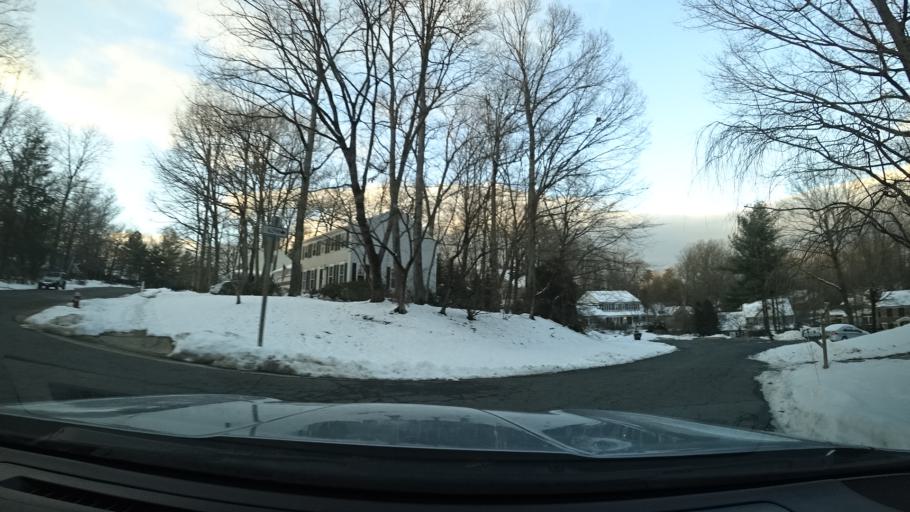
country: US
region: Virginia
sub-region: Fairfax County
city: Reston
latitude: 38.9745
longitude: -77.3461
